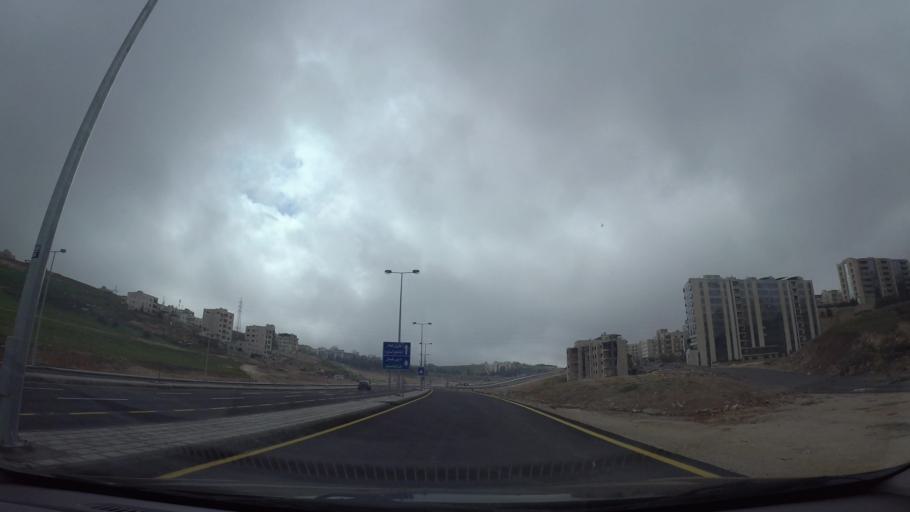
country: JO
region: Amman
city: Wadi as Sir
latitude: 31.9342
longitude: 35.8641
